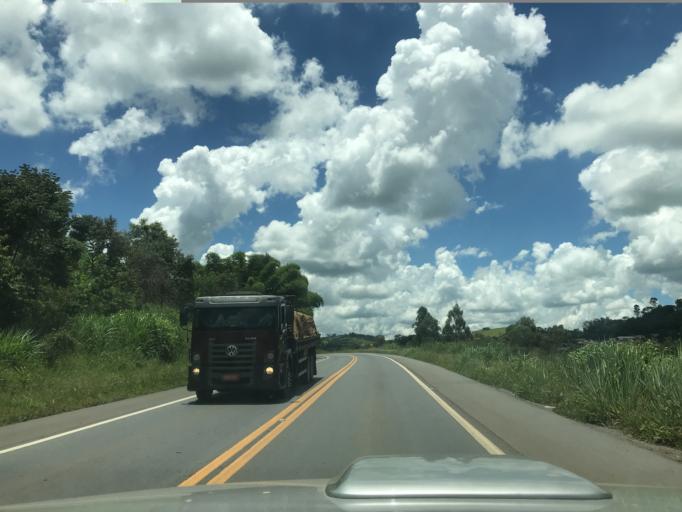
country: BR
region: Minas Gerais
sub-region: Perdoes
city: Perdoes
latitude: -21.0916
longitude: -45.0994
